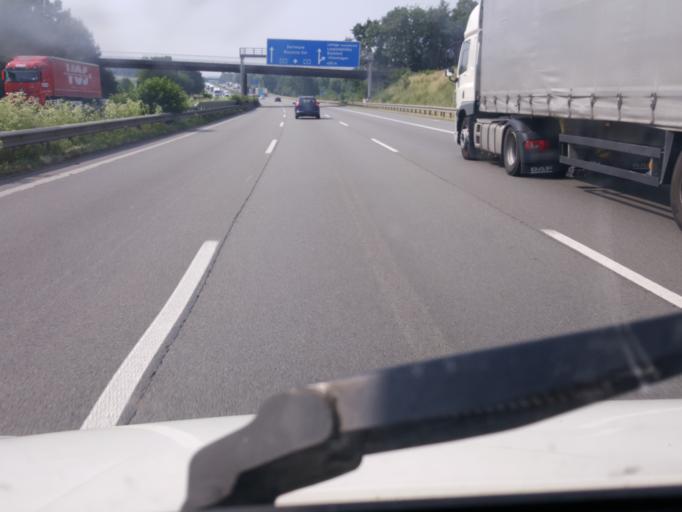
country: DE
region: North Rhine-Westphalia
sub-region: Regierungsbezirk Detmold
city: Herford
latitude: 52.0668
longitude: 8.6625
